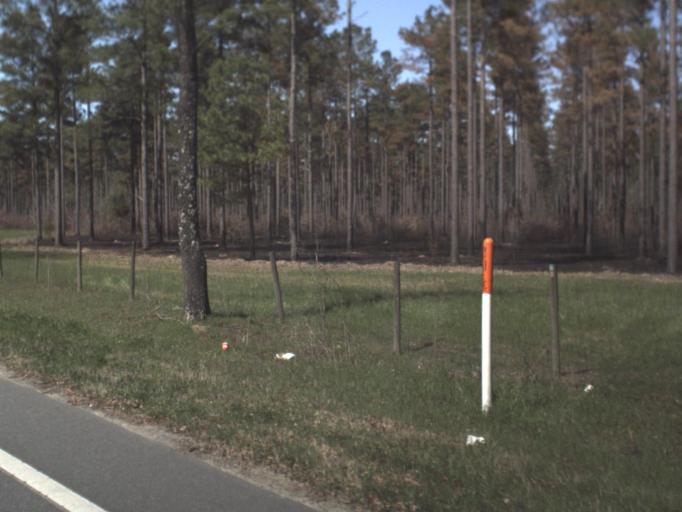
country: US
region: Florida
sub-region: Gadsden County
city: Gretna
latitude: 30.6795
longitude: -84.7093
